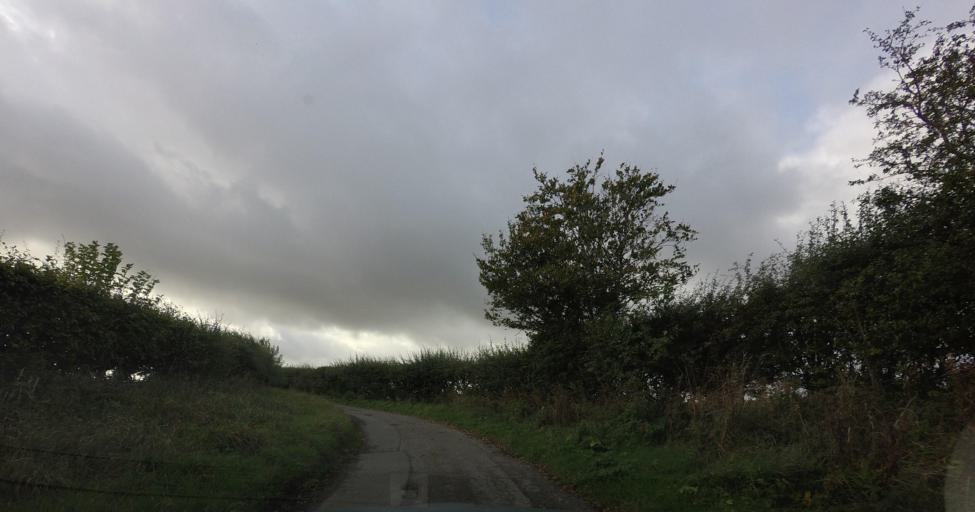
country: GB
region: Scotland
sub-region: Aberdeenshire
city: Whitehills
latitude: 57.6620
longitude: -2.6069
